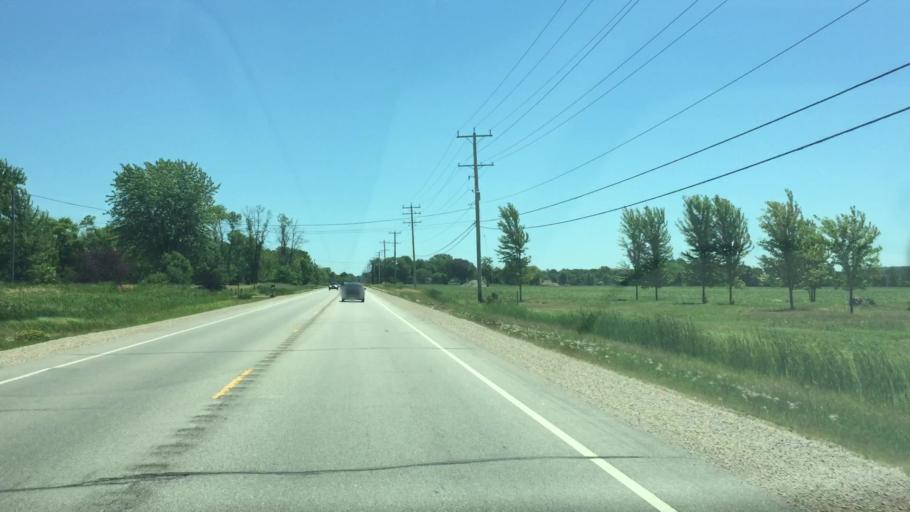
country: US
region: Wisconsin
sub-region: Calumet County
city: Sherwood
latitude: 44.1978
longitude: -88.3121
